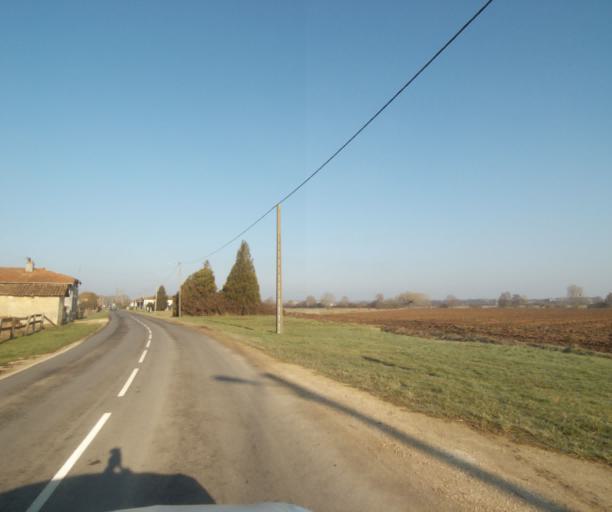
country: FR
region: Champagne-Ardenne
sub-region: Departement de la Haute-Marne
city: Montier-en-Der
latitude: 48.4578
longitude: 4.7695
